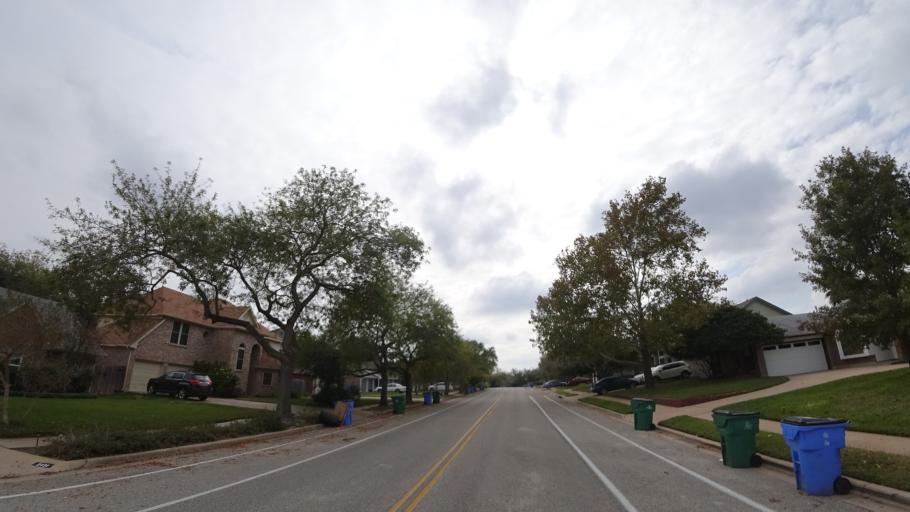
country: US
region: Texas
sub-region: Travis County
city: Wells Branch
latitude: 30.4387
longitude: -97.6817
